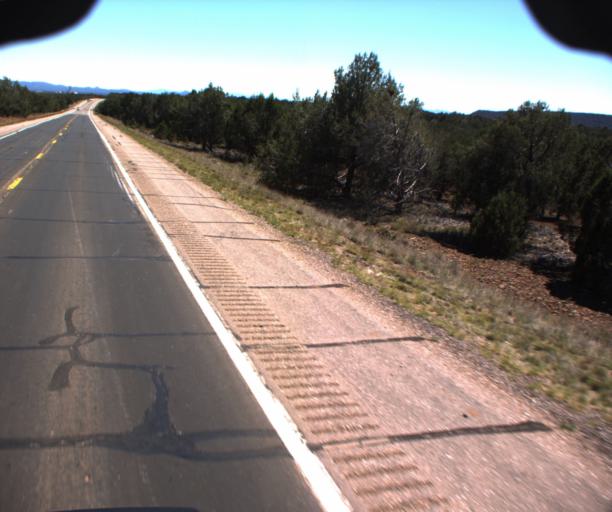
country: US
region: Arizona
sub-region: Yavapai County
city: Paulden
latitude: 35.0564
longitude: -112.3978
